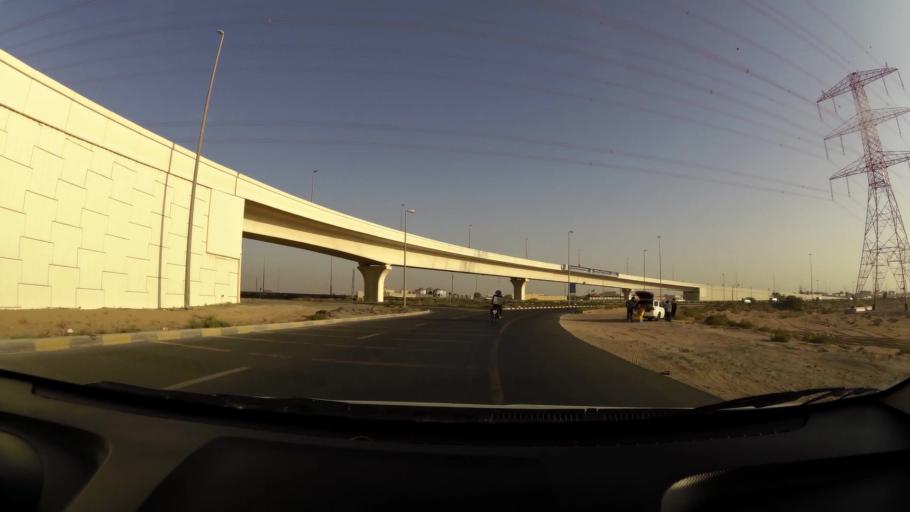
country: AE
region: Ajman
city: Ajman
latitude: 25.3602
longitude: 55.5139
